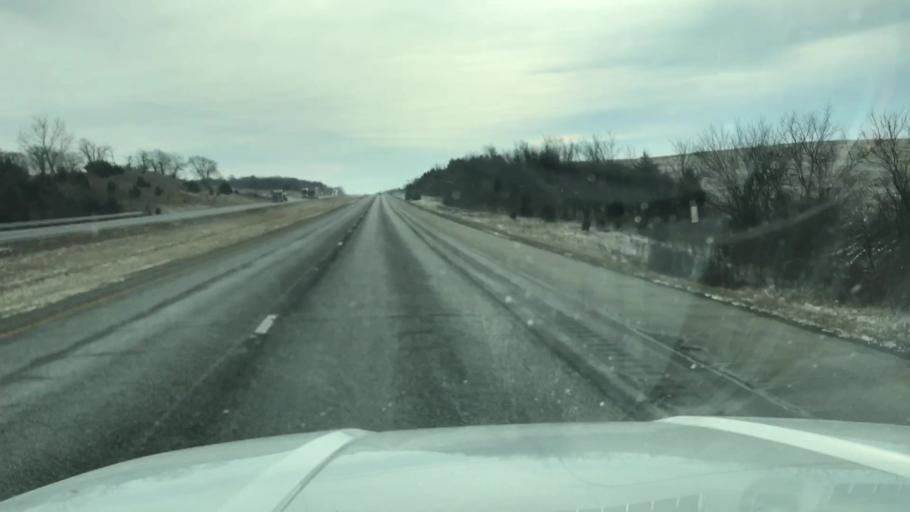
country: US
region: Missouri
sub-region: Holt County
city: Oregon
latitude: 39.9857
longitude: -95.0374
